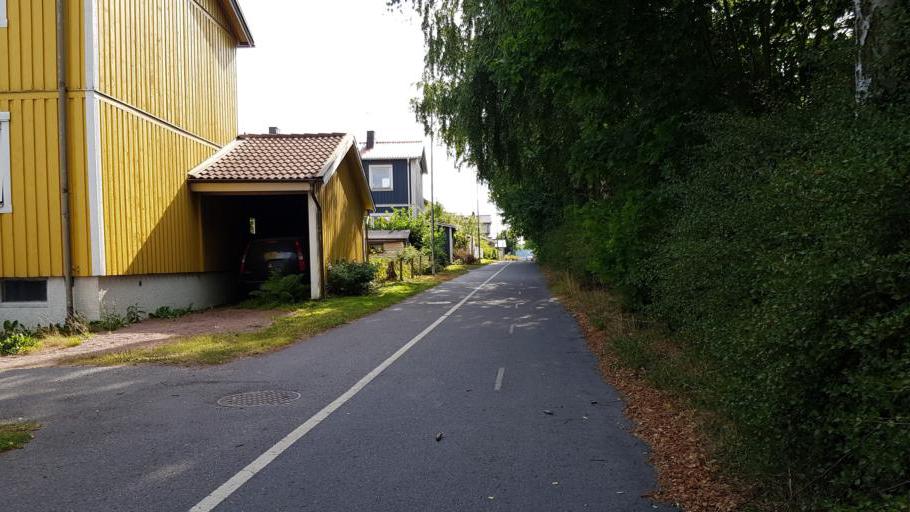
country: SE
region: Vaestra Goetaland
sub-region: Goteborg
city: Eriksbo
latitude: 57.7281
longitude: 12.0447
